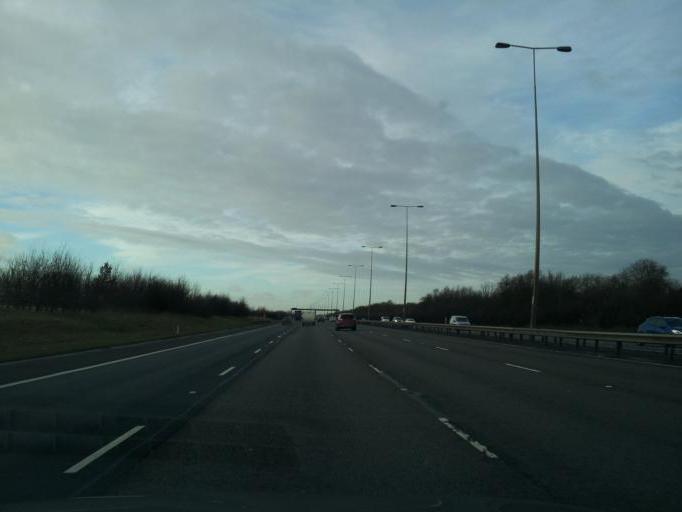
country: GB
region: England
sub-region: Cambridgeshire
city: Stilton
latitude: 52.4680
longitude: -0.2835
